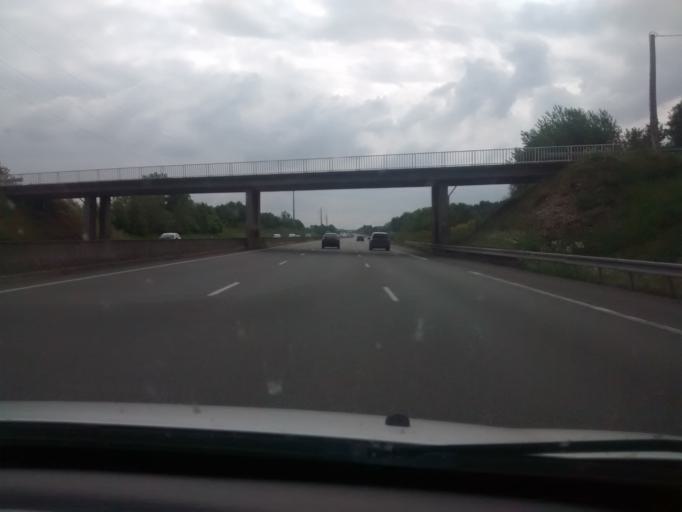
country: FR
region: Centre
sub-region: Departement d'Eure-et-Loir
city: Yevres
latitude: 48.2837
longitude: 1.2403
